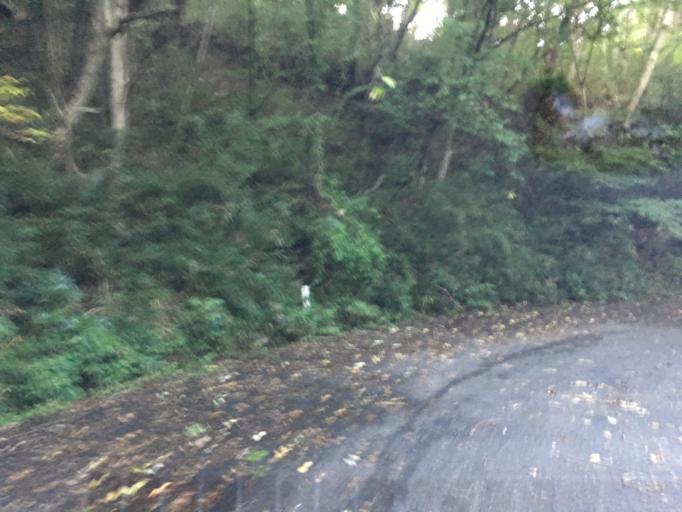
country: JP
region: Fukushima
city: Yanagawamachi-saiwaicho
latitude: 37.8944
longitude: 140.5458
